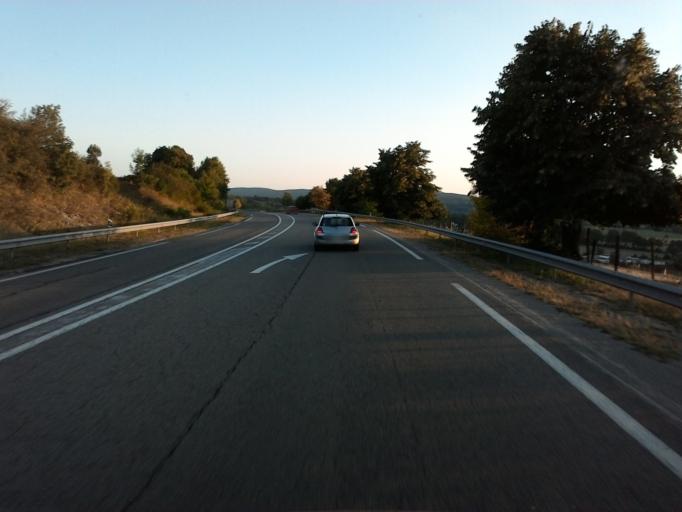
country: FR
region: Franche-Comte
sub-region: Departement du Doubs
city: Quingey
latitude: 47.1008
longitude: 5.8967
